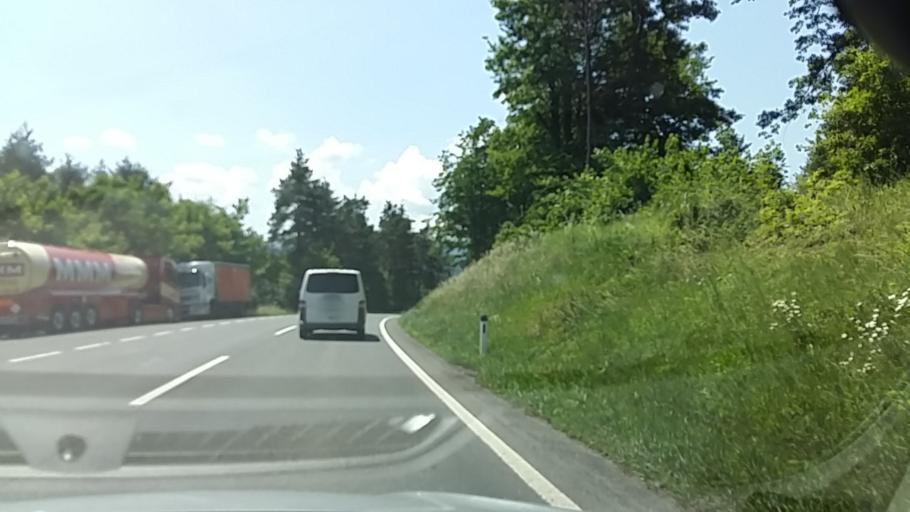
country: AT
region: Burgenland
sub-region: Politischer Bezirk Oberpullendorf
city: Lockenhaus
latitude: 47.4187
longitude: 16.3921
